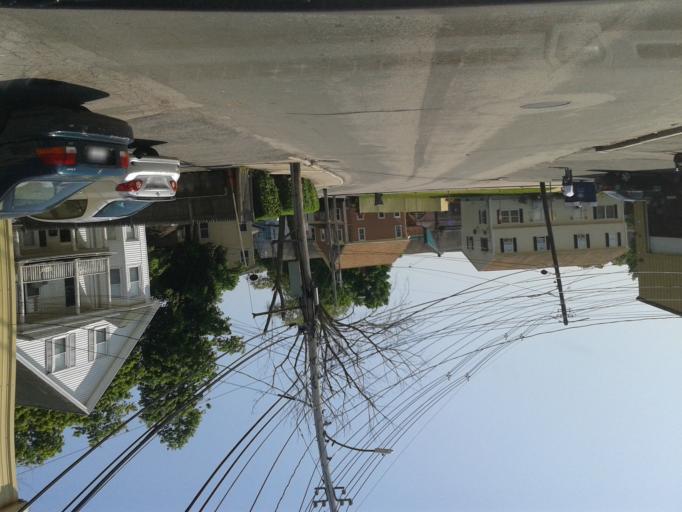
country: US
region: Massachusetts
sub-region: Middlesex County
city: Framingham
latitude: 42.2752
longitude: -71.4207
